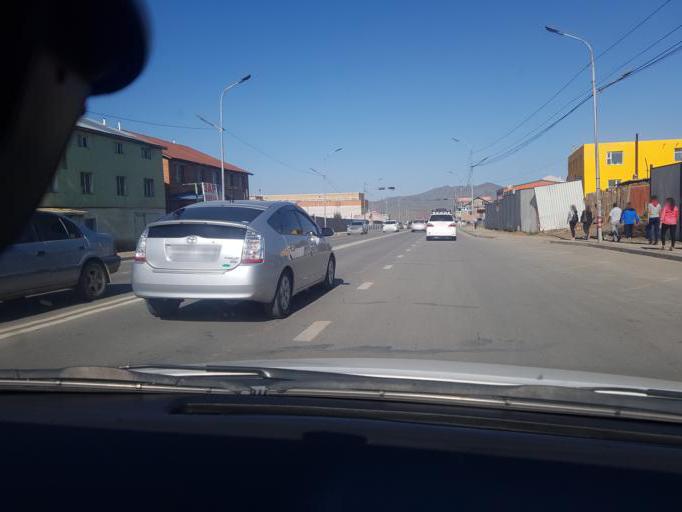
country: MN
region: Ulaanbaatar
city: Ulaanbaatar
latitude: 47.9541
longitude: 106.8514
